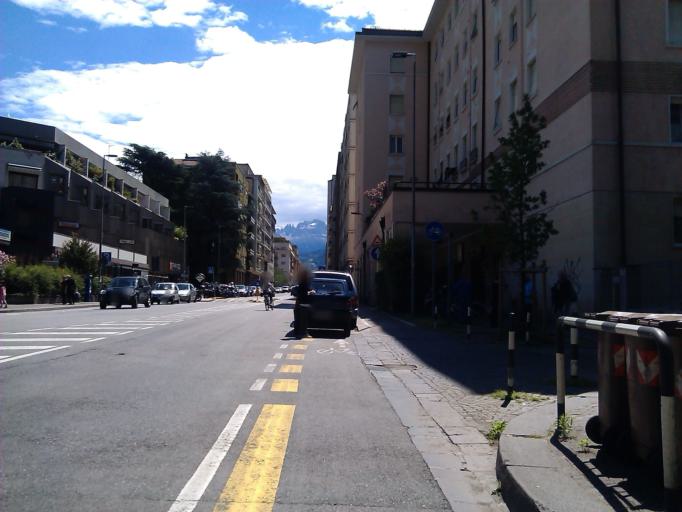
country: IT
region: Trentino-Alto Adige
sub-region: Bolzano
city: Bolzano
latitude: 46.5022
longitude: 11.3363
